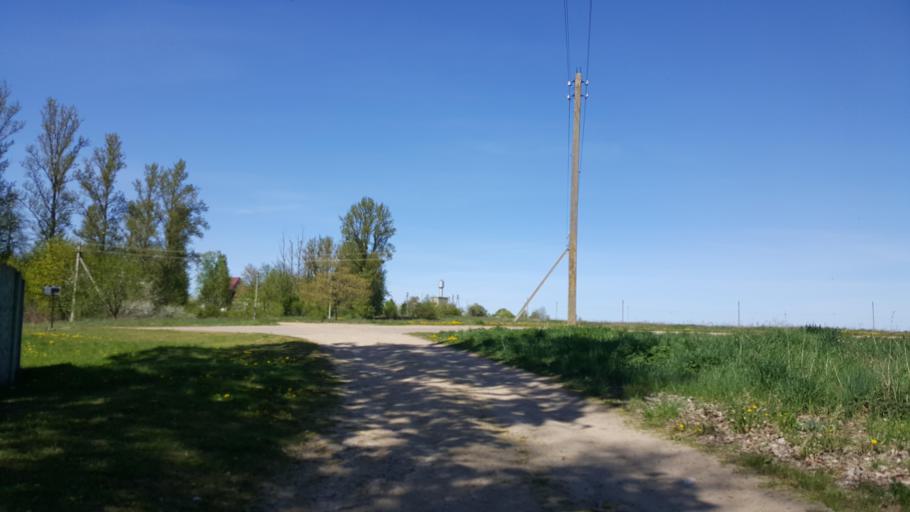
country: BY
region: Brest
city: Kamyanyets
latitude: 52.4385
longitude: 23.8486
